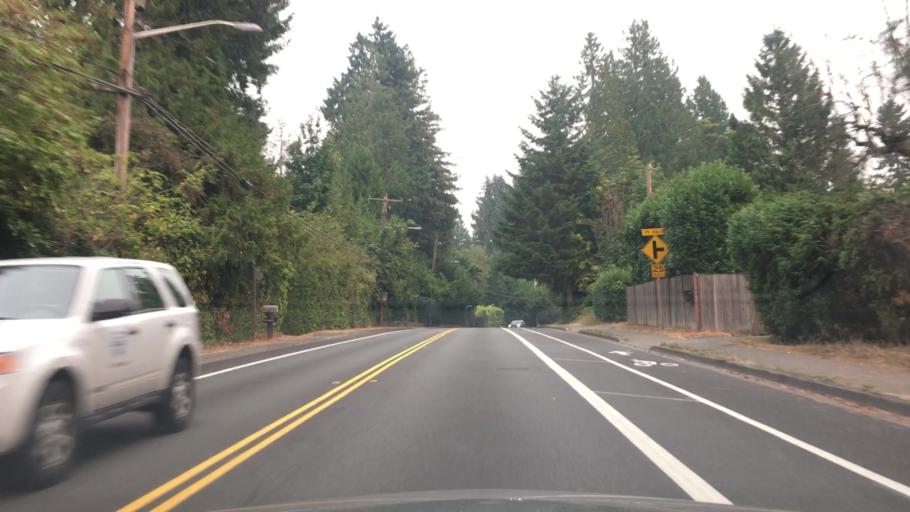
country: US
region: Washington
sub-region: King County
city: Kenmore
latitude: 47.7515
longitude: -122.2421
